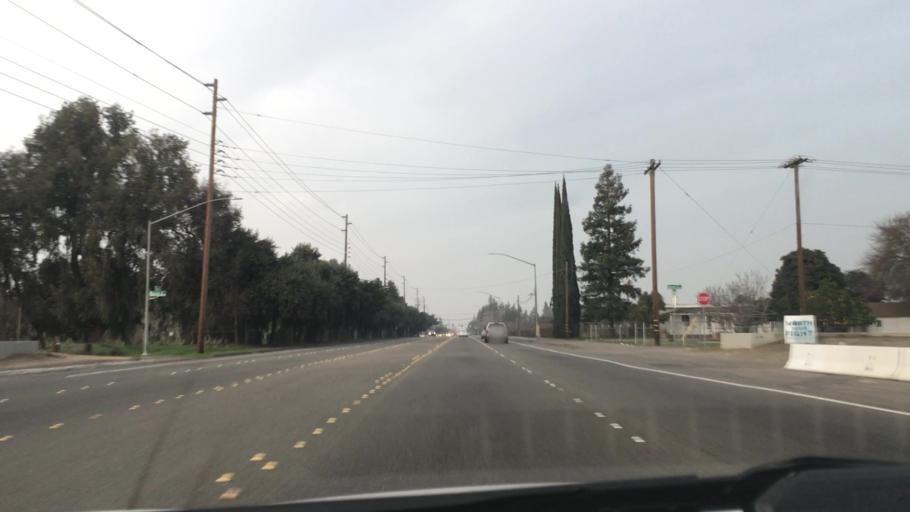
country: US
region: California
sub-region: Stanislaus County
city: Empire
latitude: 37.6521
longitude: -120.9211
